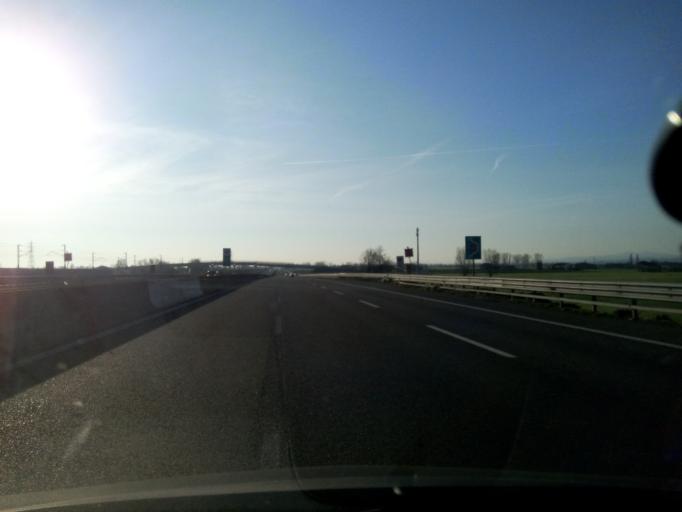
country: IT
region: Emilia-Romagna
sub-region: Provincia di Piacenza
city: Alseno
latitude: 44.9213
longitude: 9.9969
